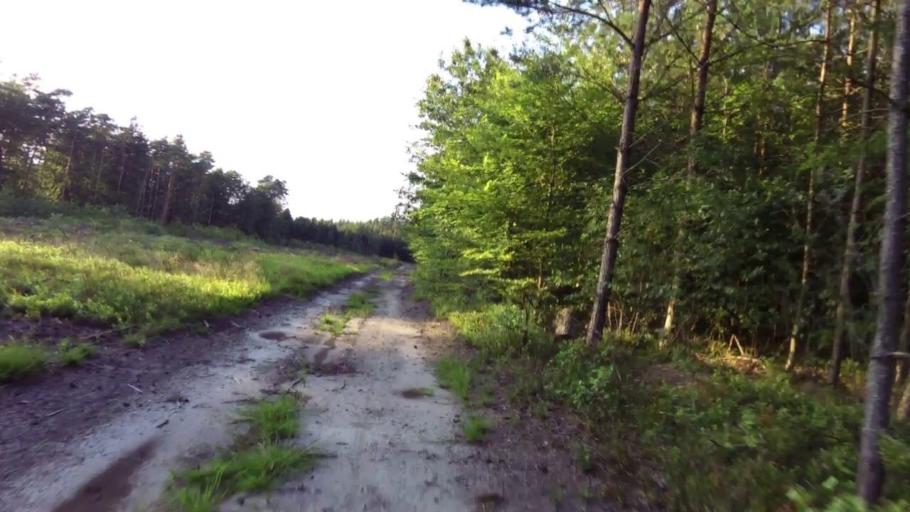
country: PL
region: West Pomeranian Voivodeship
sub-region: Powiat drawski
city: Zlocieniec
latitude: 53.5544
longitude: 16.0178
